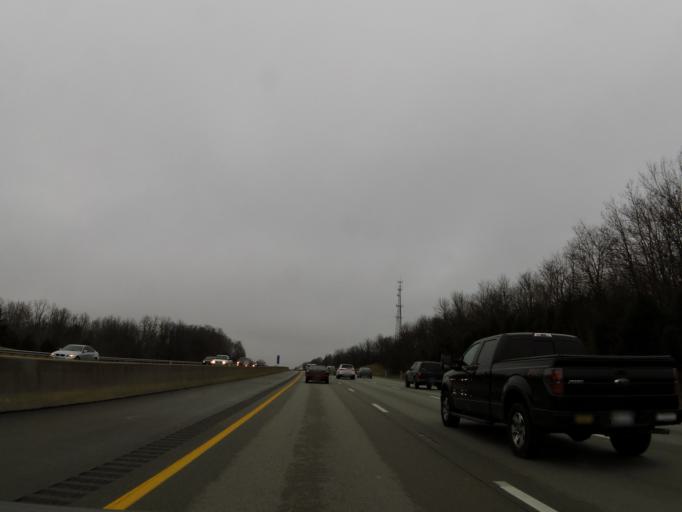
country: US
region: Kentucky
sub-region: Scott County
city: Georgetown
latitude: 38.3145
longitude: -84.5583
